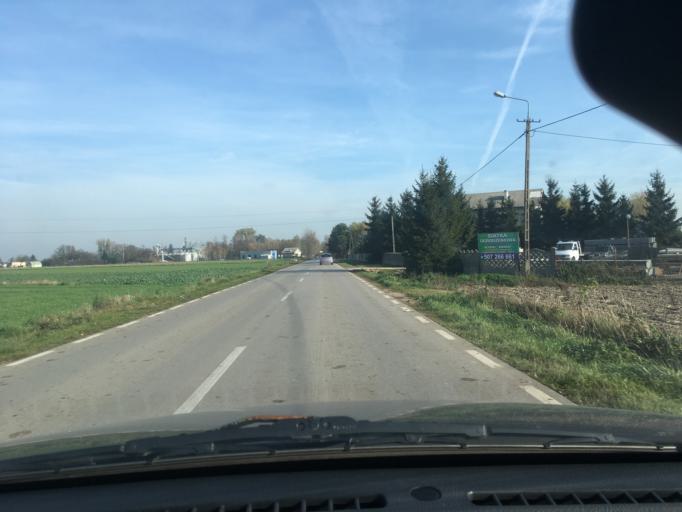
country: PL
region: Masovian Voivodeship
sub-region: Powiat plocki
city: Bodzanow
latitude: 52.4892
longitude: 20.0223
